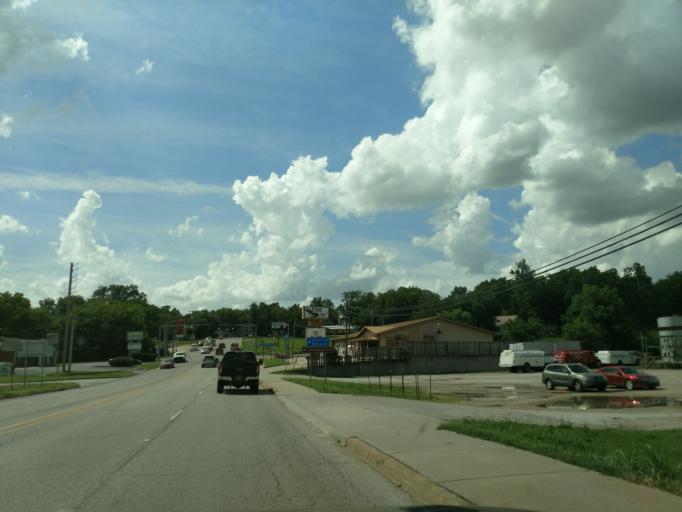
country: US
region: Arkansas
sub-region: Carroll County
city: Berryville
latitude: 36.3601
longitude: -93.5630
